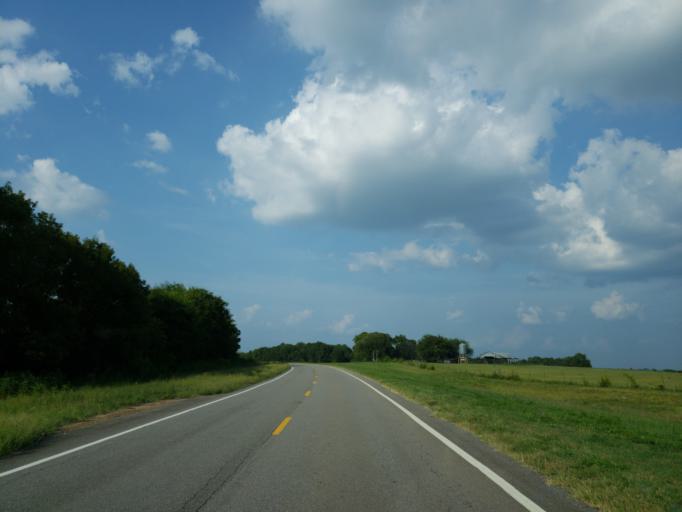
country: US
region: Alabama
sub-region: Greene County
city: Eutaw
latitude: 32.7803
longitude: -87.9806
